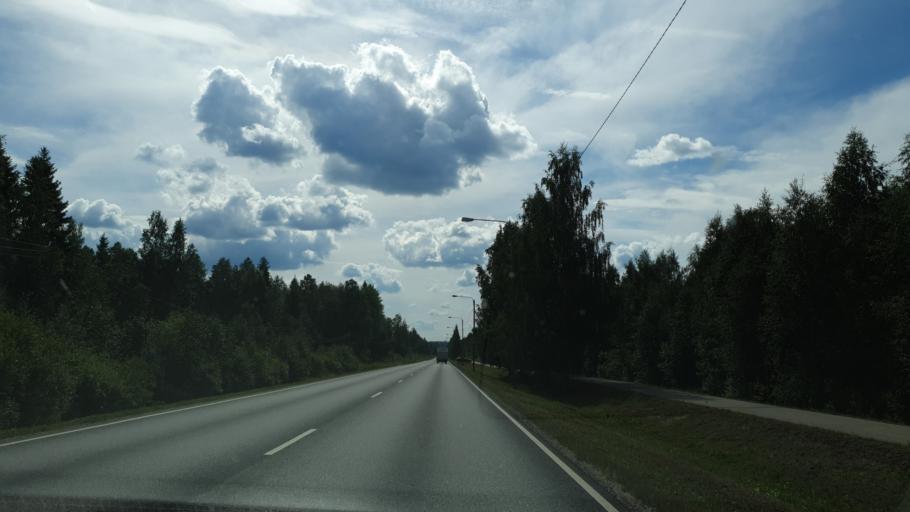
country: FI
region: Kainuu
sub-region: Kajaani
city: Sotkamo
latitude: 64.1634
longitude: 28.4410
